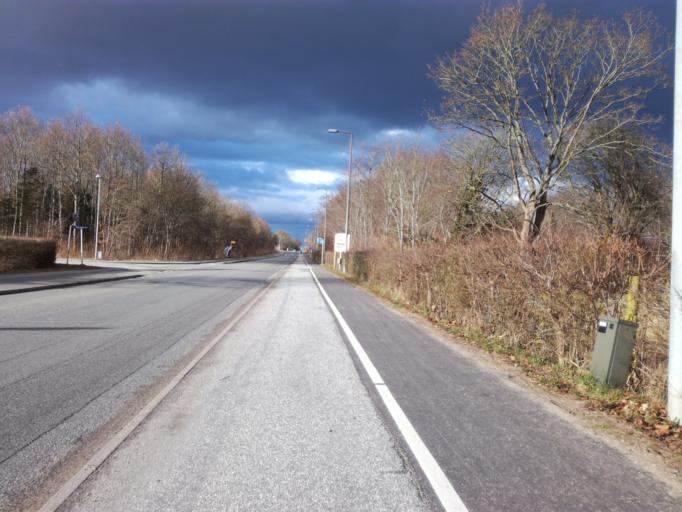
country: DK
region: South Denmark
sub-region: Fredericia Kommune
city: Fredericia
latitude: 55.5846
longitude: 9.7673
